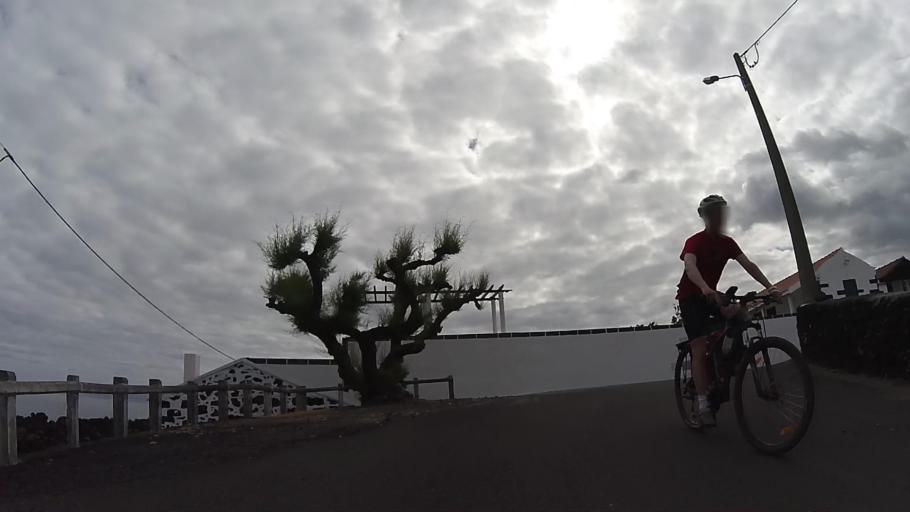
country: PT
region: Azores
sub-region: Madalena
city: Madalena
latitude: 38.5560
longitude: -28.4465
